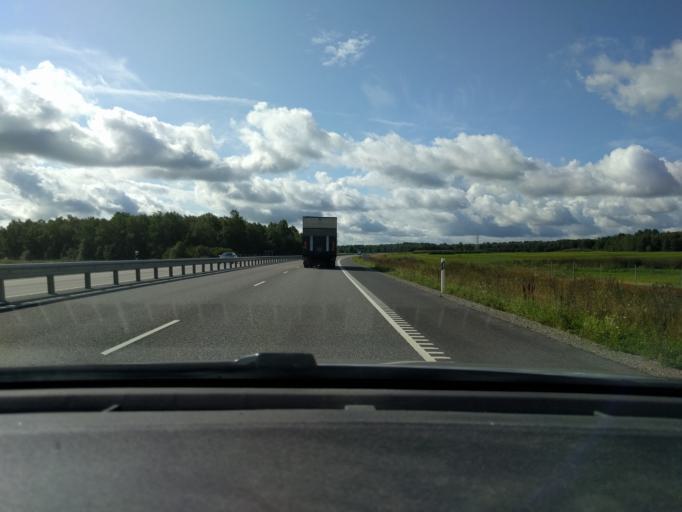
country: EE
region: Harju
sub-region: Rae vald
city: Jueri
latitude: 59.3892
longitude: 24.9197
